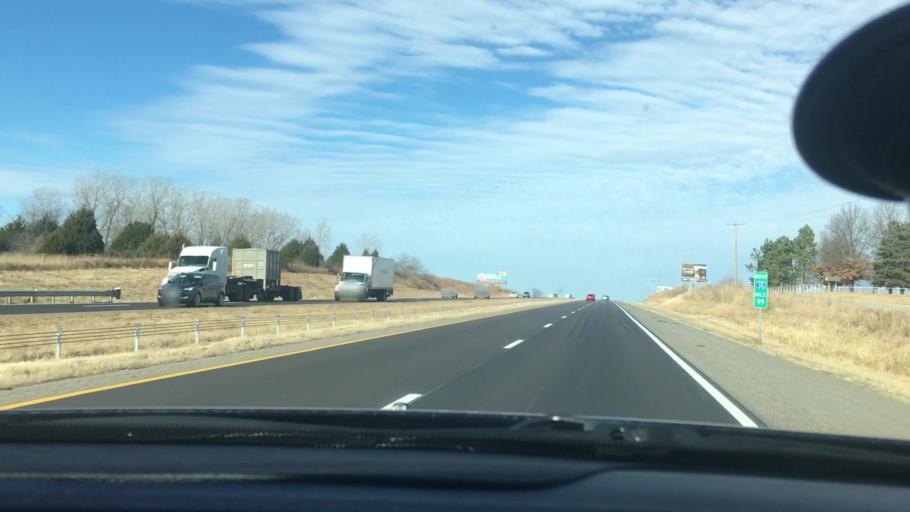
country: US
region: Oklahoma
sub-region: Cleveland County
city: Noble
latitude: 35.0889
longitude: -97.4171
